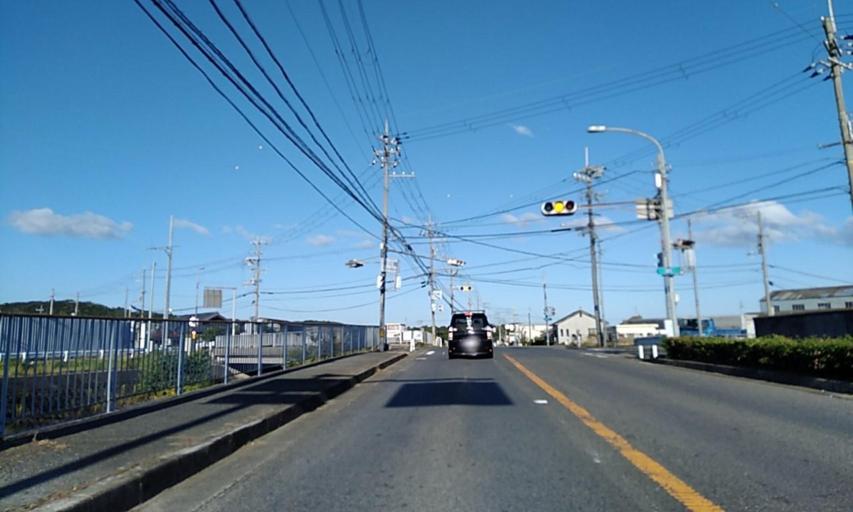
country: JP
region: Wakayama
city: Wakayama-shi
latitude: 34.3175
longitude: 135.1242
